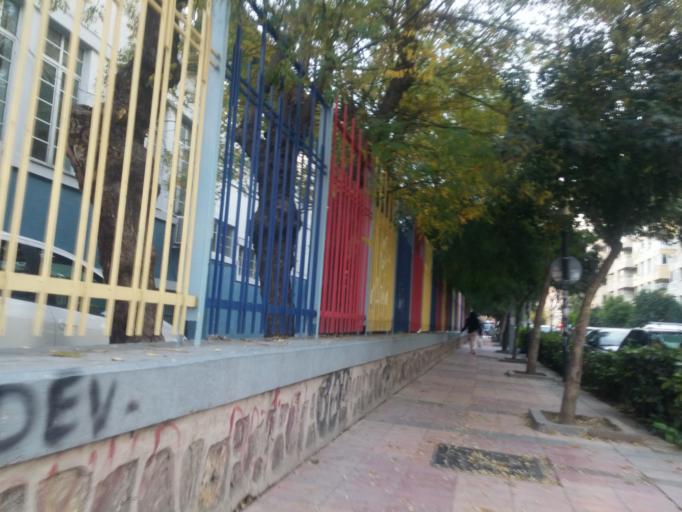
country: TR
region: Izmir
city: Izmir
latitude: 38.4339
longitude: 27.1408
